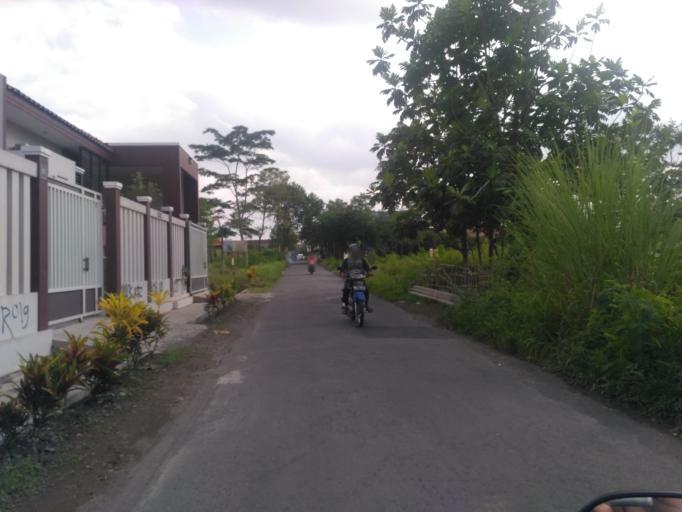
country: ID
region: Daerah Istimewa Yogyakarta
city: Yogyakarta
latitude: -7.7692
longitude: 110.3589
